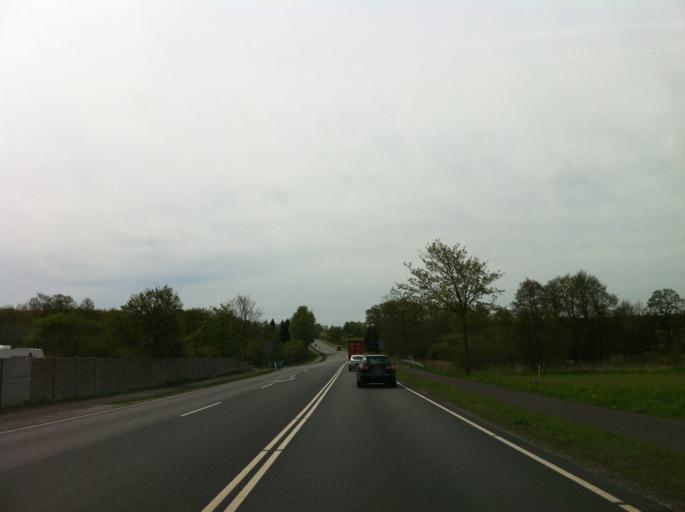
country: DK
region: Zealand
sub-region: Lejre Kommune
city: Osted
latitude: 55.5315
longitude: 11.9157
